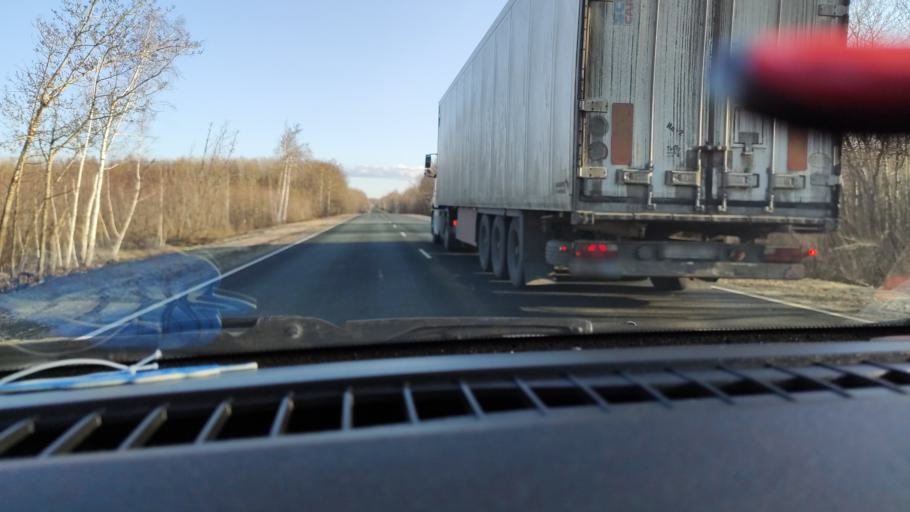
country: RU
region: Saratov
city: Khvalynsk
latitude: 52.4289
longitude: 48.0087
